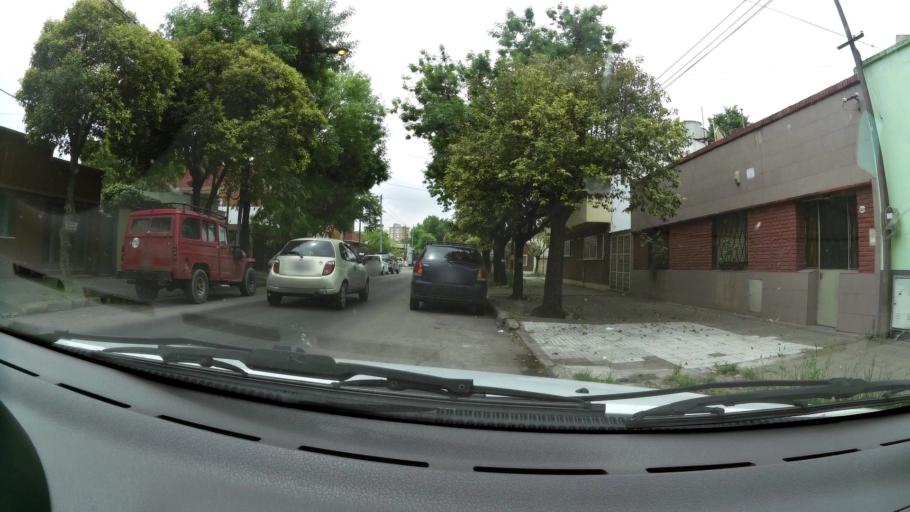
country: AR
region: Buenos Aires
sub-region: Partido de La Plata
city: La Plata
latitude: -34.9308
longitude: -57.9685
